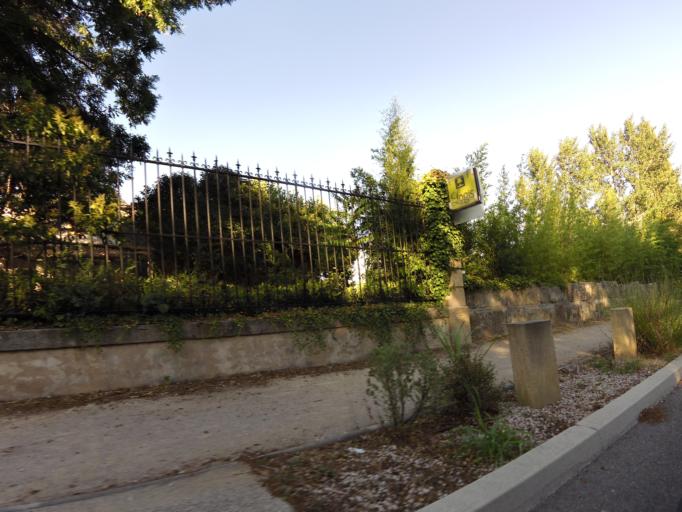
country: FR
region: Languedoc-Roussillon
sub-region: Departement du Gard
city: Castillon-du-Gard
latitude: 43.9461
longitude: 4.5483
